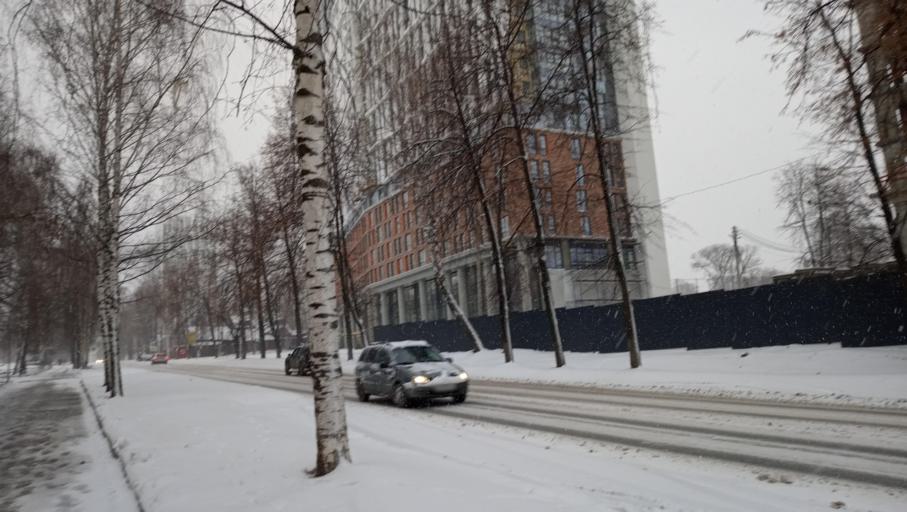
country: RU
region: Udmurtiya
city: Izhevsk
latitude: 56.8618
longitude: 53.2020
